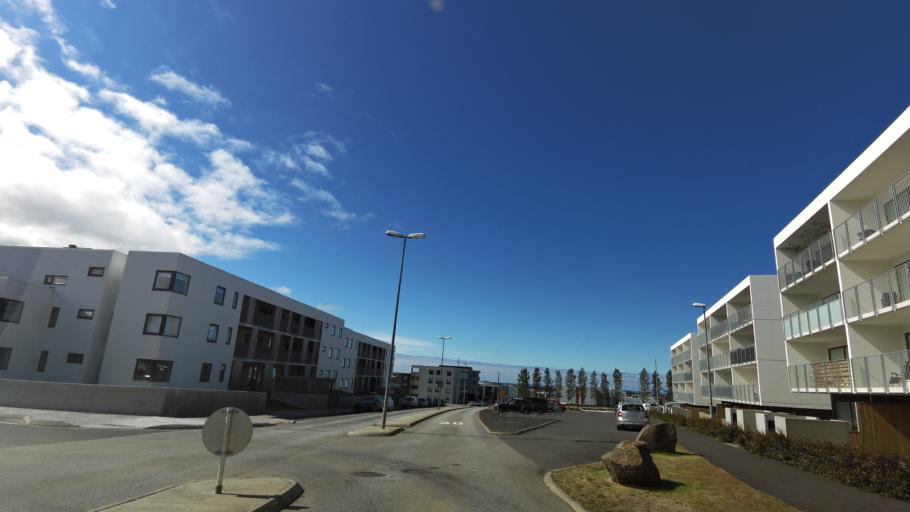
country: IS
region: Capital Region
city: Mosfellsbaer
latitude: 64.1673
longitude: -21.6625
